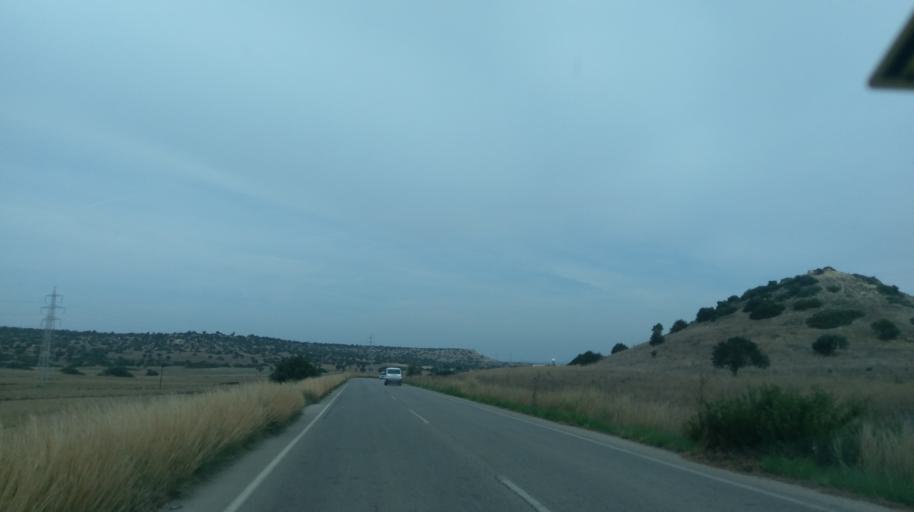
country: CY
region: Ammochostos
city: Leonarisso
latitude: 35.3927
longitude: 34.0601
